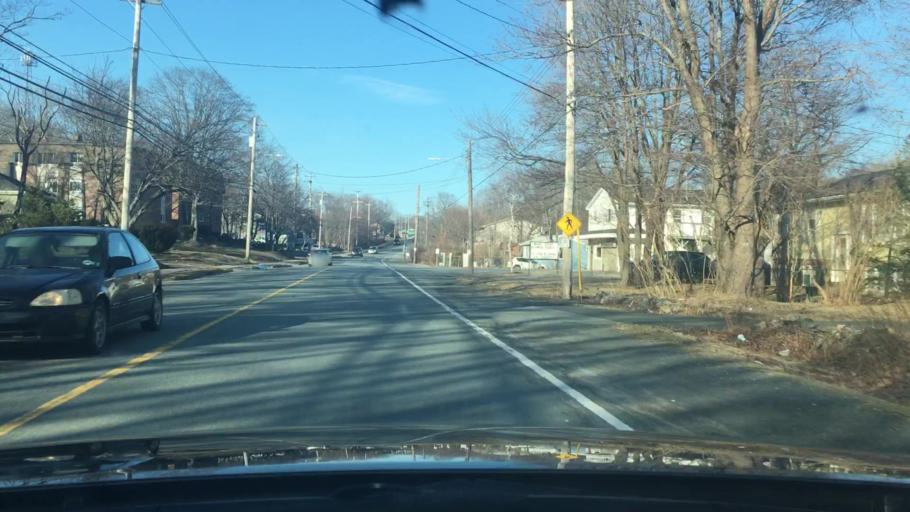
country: CA
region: Nova Scotia
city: Dartmouth
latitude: 44.7395
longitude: -63.6445
